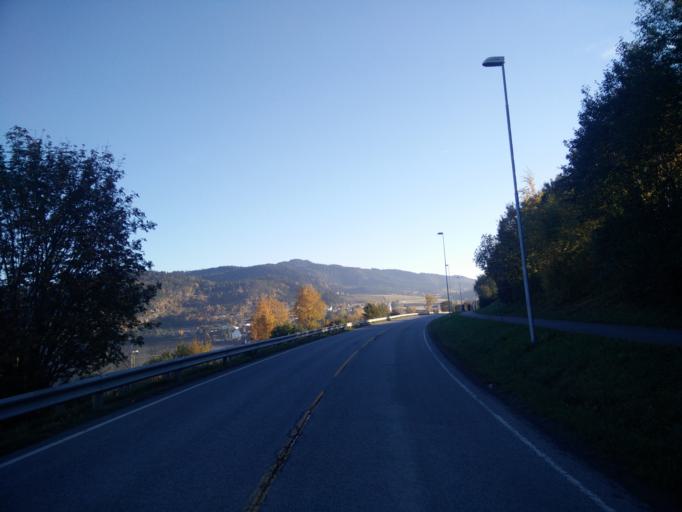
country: NO
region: Sor-Trondelag
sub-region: Skaun
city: Borsa
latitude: 63.3317
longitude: 10.0695
